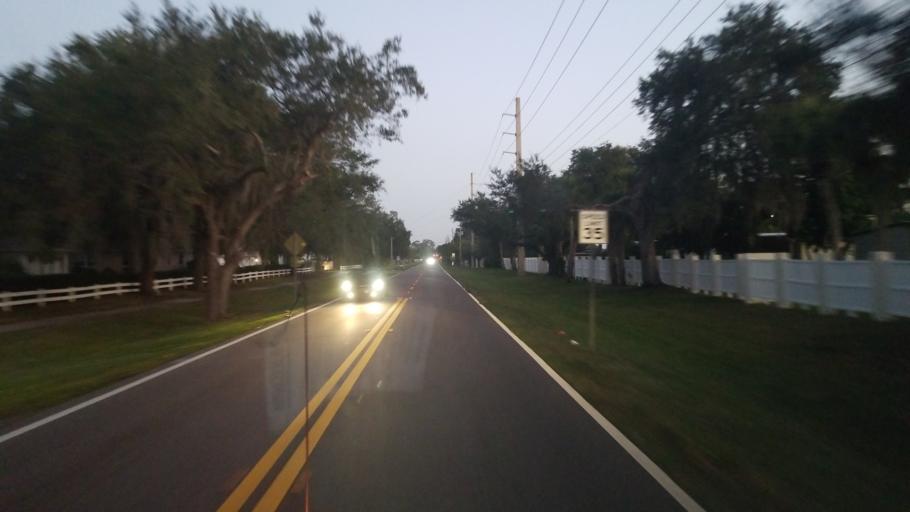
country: US
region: Florida
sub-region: Sarasota County
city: Lake Sarasota
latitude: 27.2769
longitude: -82.4564
